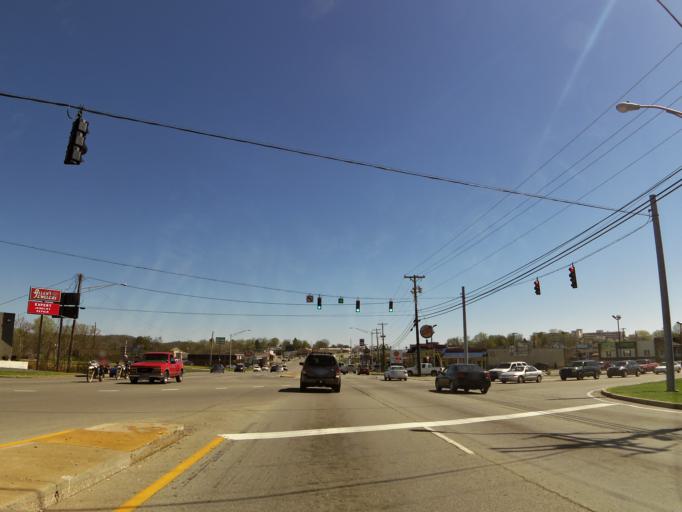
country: US
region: Kentucky
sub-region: Pulaski County
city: Somerset
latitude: 37.0944
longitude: -84.6192
